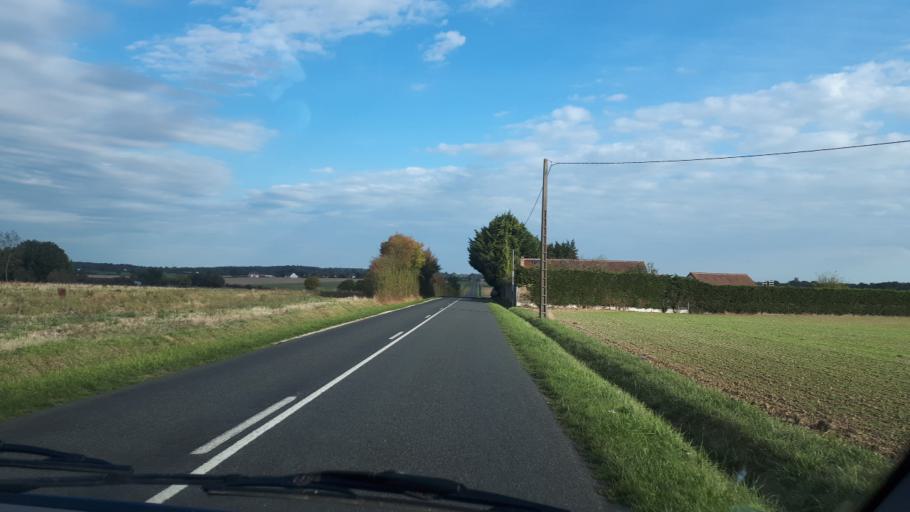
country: FR
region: Centre
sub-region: Departement du Loir-et-Cher
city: Sarge-sur-Braye
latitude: 47.9060
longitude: 0.9303
